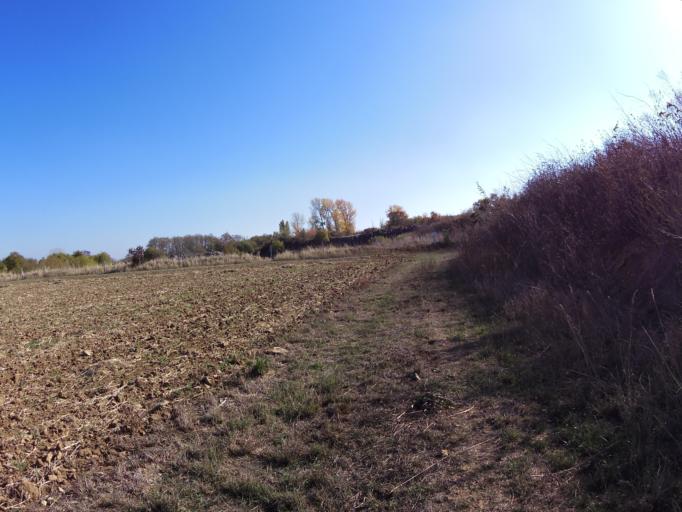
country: DE
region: Bavaria
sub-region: Regierungsbezirk Unterfranken
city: Eibelstadt
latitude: 49.7133
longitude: 9.9888
